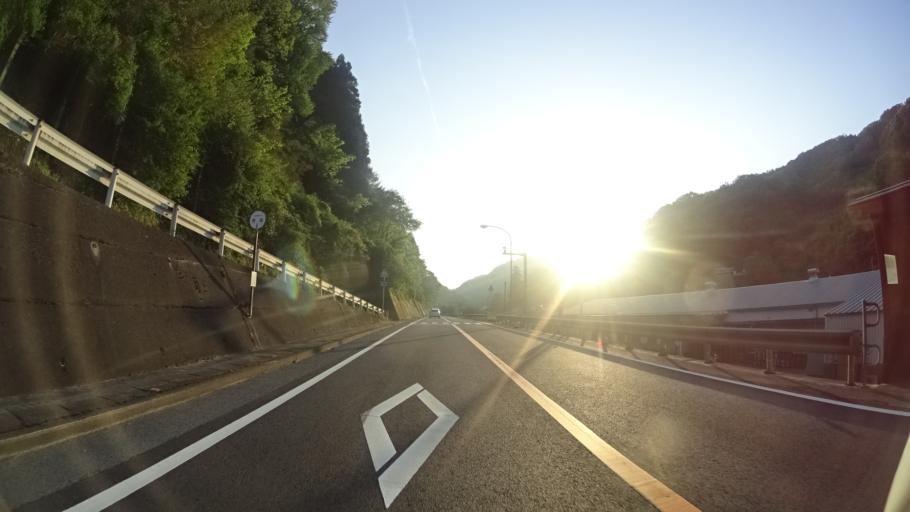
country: JP
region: Tokushima
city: Ikedacho
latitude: 34.0101
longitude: 133.7419
